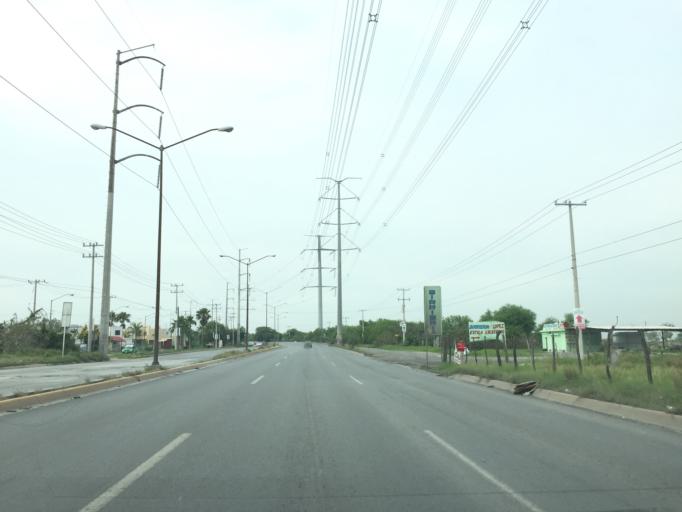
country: MX
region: Nuevo Leon
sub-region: Apodaca
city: Fraccionamiento Cosmopolis Octavo Sector
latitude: 25.7859
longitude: -100.2240
